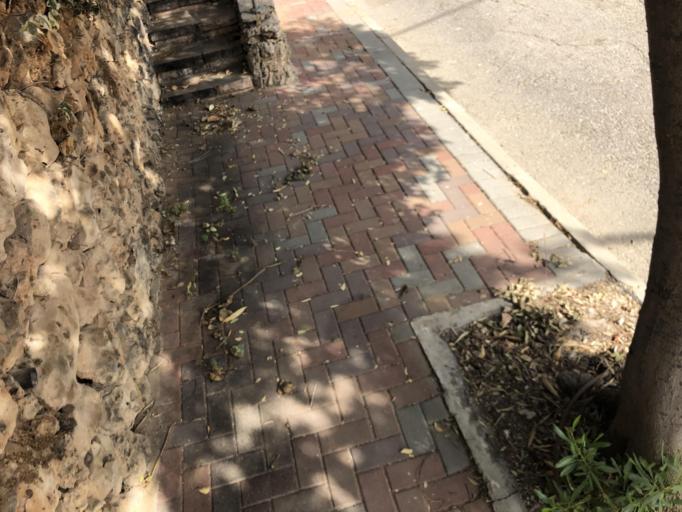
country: PS
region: West Bank
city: Jit
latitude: 32.2126
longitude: 35.1577
